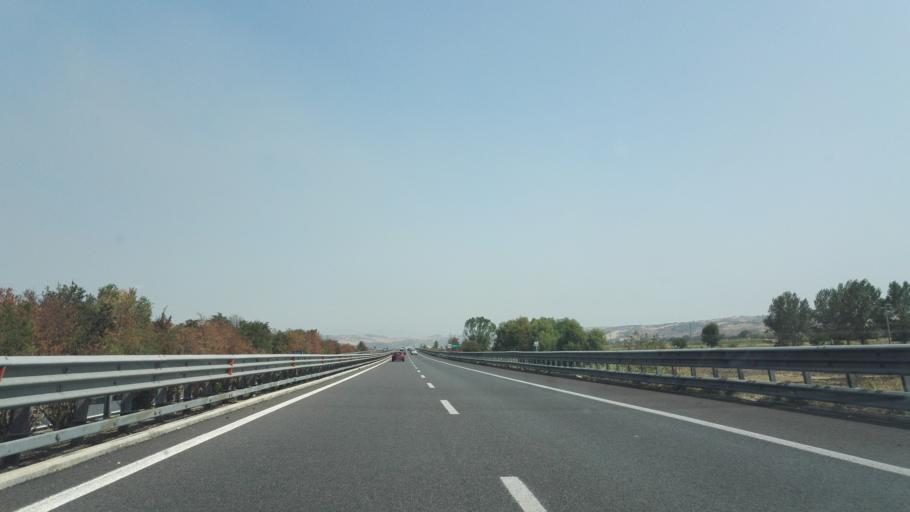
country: IT
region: Calabria
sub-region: Provincia di Cosenza
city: Sartano
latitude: 39.5456
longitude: 16.2276
